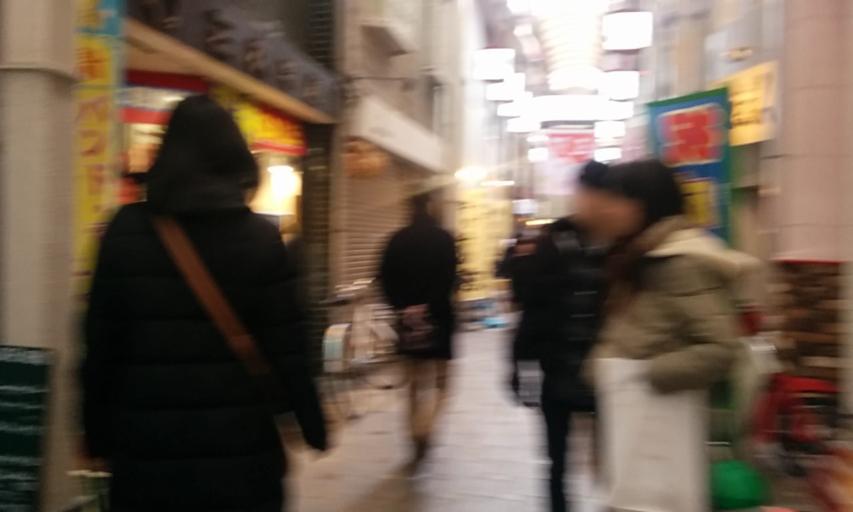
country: JP
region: Kyoto
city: Kyoto
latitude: 35.0043
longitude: 135.7677
